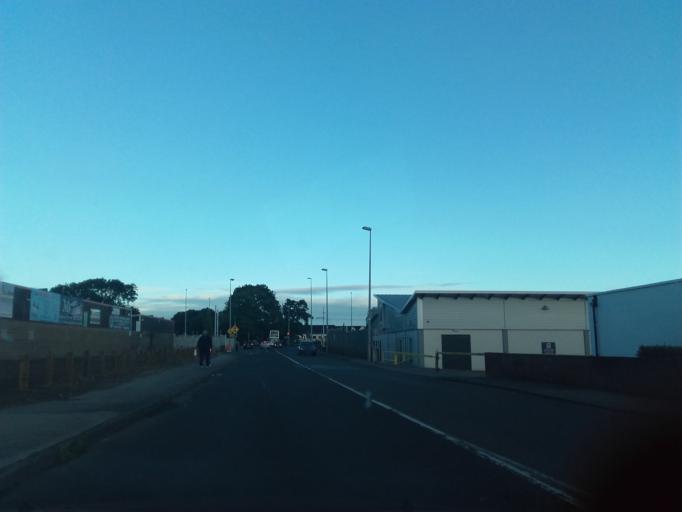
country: IE
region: Leinster
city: Tallaght
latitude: 53.2987
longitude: -6.3730
